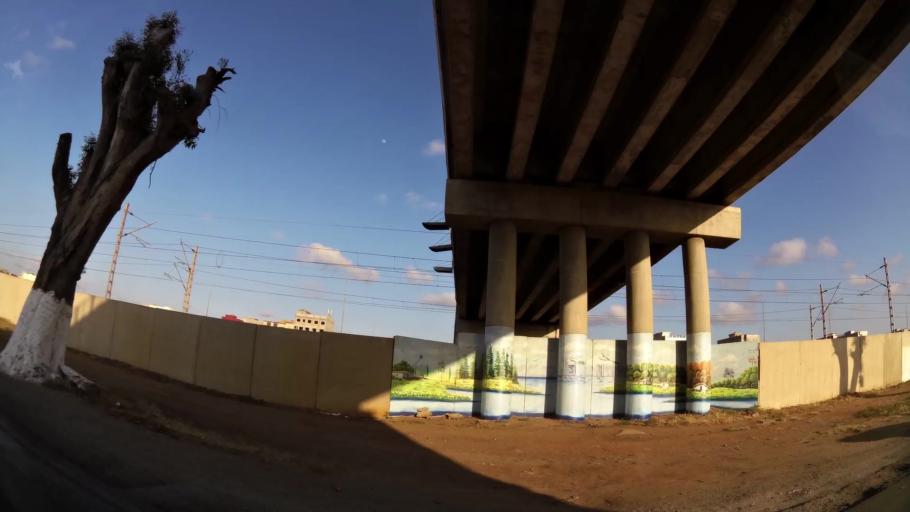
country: MA
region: Rabat-Sale-Zemmour-Zaer
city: Sale
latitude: 34.0794
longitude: -6.7786
